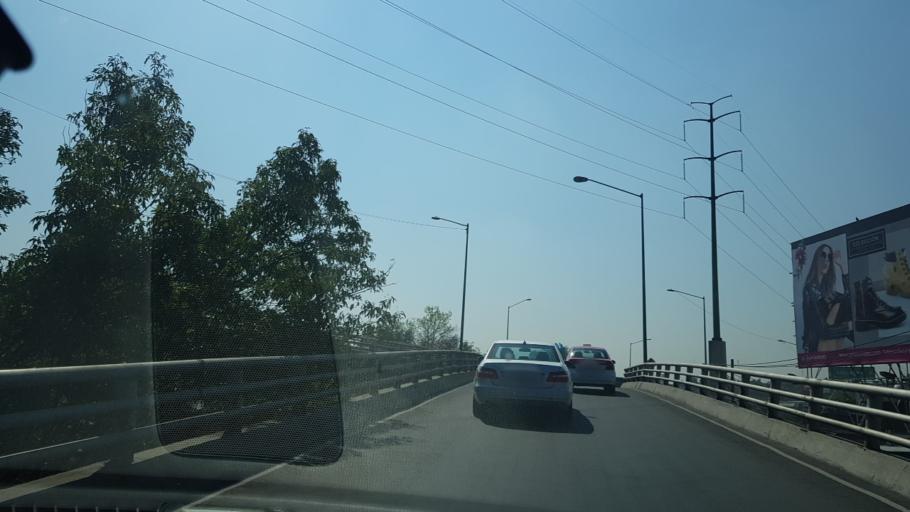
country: MX
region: Mexico City
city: Alvaro Obregon
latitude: 19.3820
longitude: -99.2003
